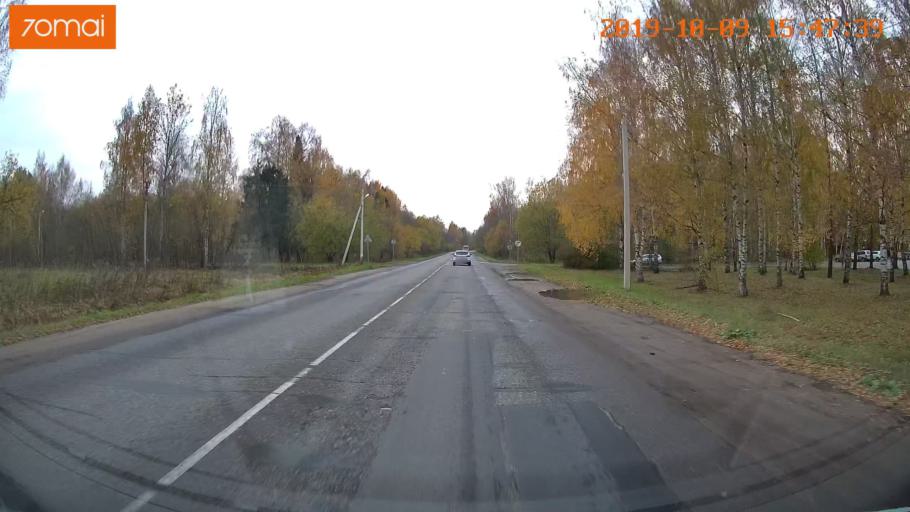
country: RU
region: Kostroma
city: Oktyabr'skiy
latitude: 57.8161
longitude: 41.0257
